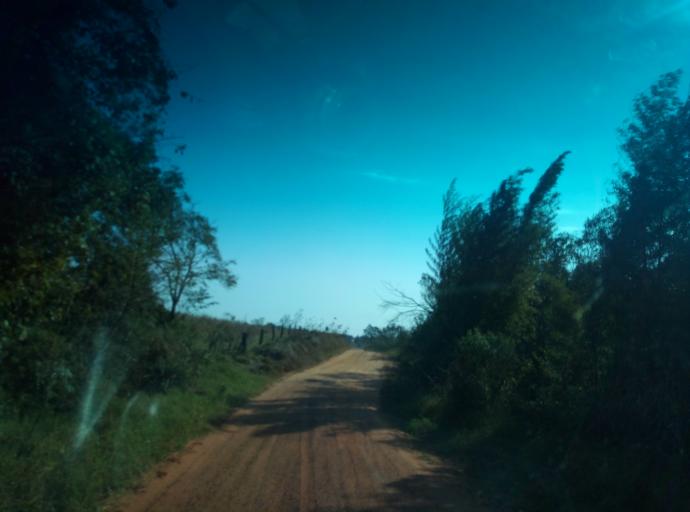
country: PY
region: Caaguazu
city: Doctor Cecilio Baez
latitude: -25.1649
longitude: -56.2176
